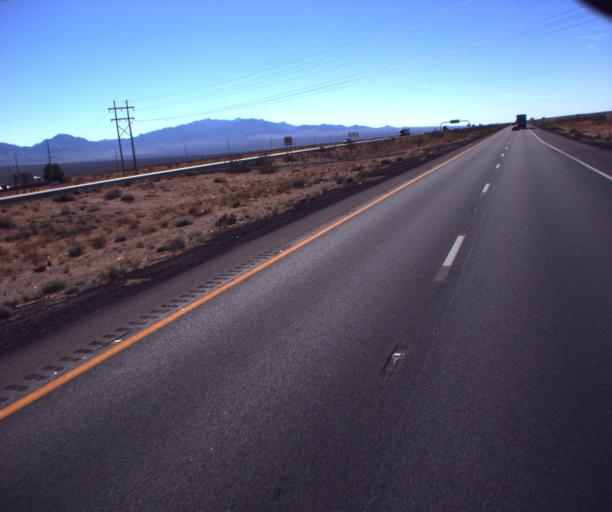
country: US
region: Arizona
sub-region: Mohave County
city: Beaver Dam
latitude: 36.8871
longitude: -113.9373
